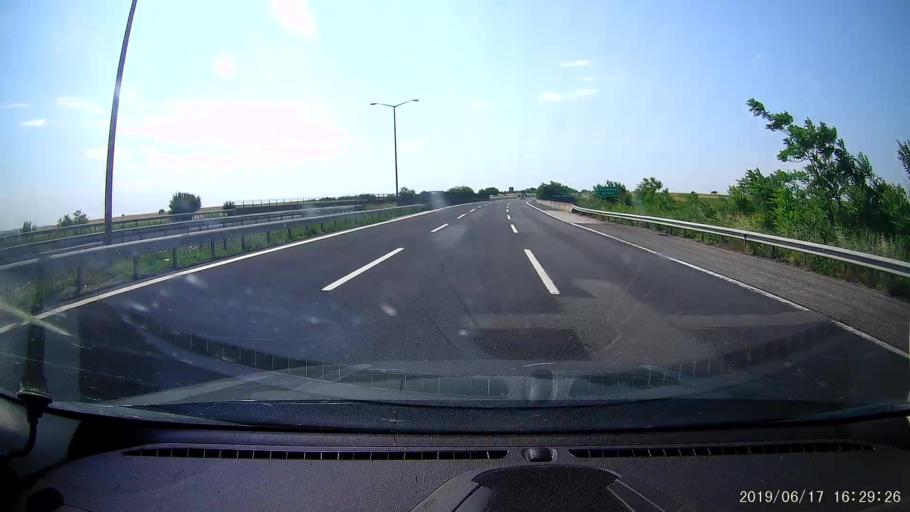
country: TR
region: Tekirdag
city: Beyazkoy
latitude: 41.3336
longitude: 27.6815
